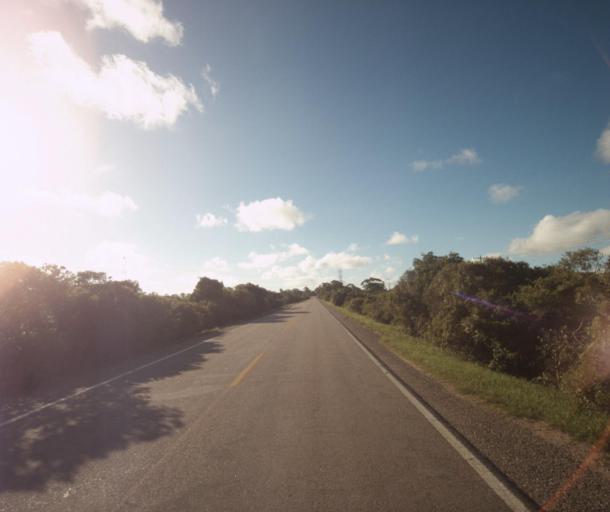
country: BR
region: Rio Grande do Sul
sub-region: Arroio Grande
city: Arroio Grande
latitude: -32.5035
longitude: -52.5715
